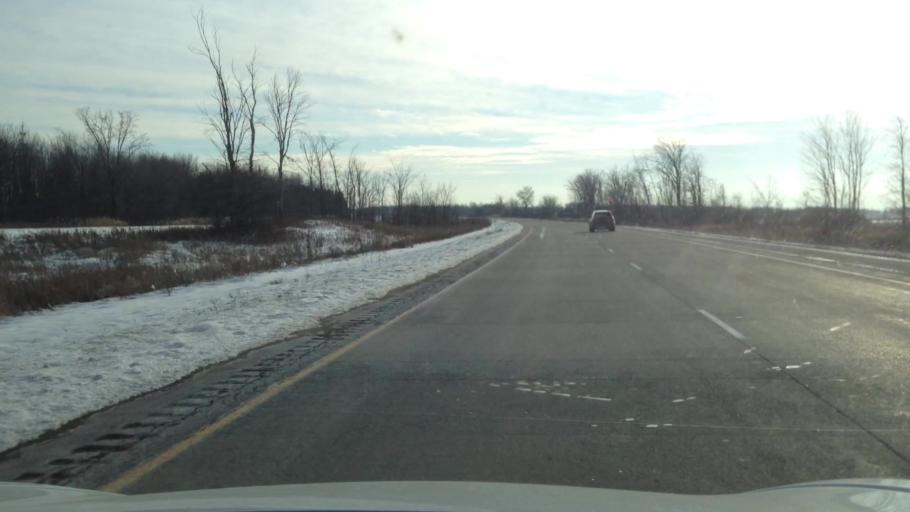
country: CA
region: Ontario
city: Hawkesbury
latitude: 45.4180
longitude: -74.7680
